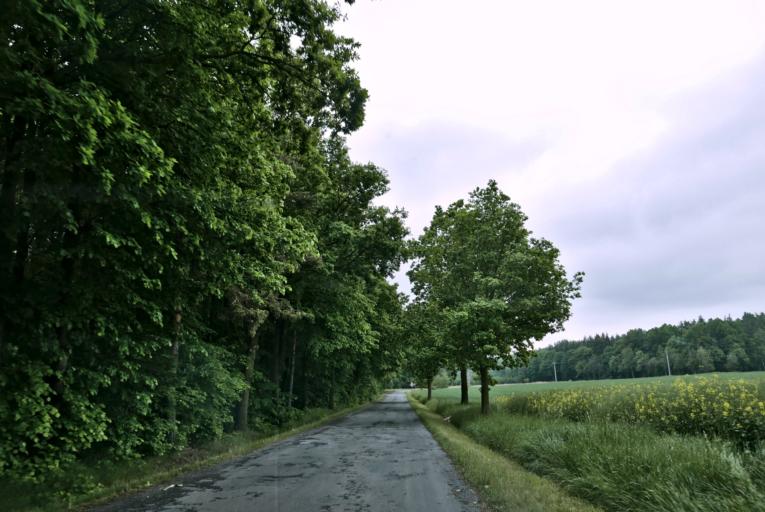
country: CZ
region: Plzensky
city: Kralovice
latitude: 49.9856
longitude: 13.4263
